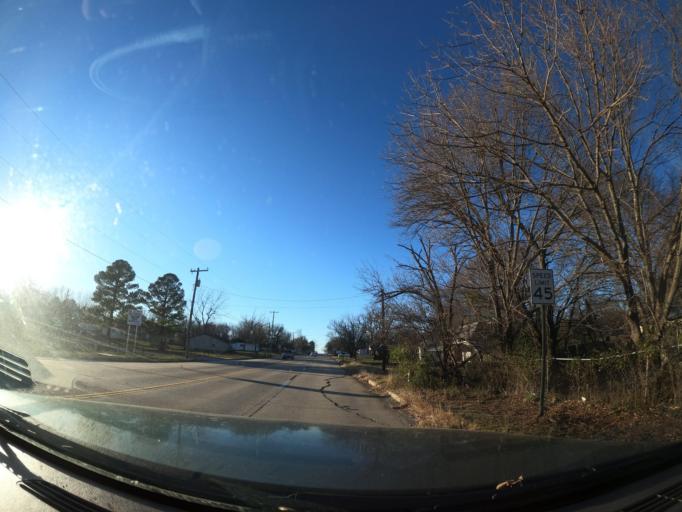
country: US
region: Oklahoma
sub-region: Pittsburg County
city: Hartshorne
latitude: 34.8421
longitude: -95.5464
